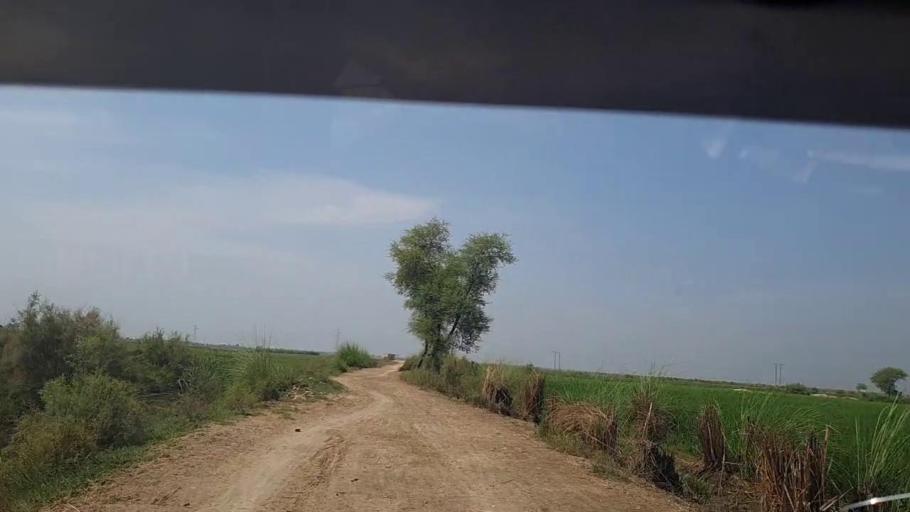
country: PK
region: Sindh
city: Thul
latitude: 28.2190
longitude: 68.6766
